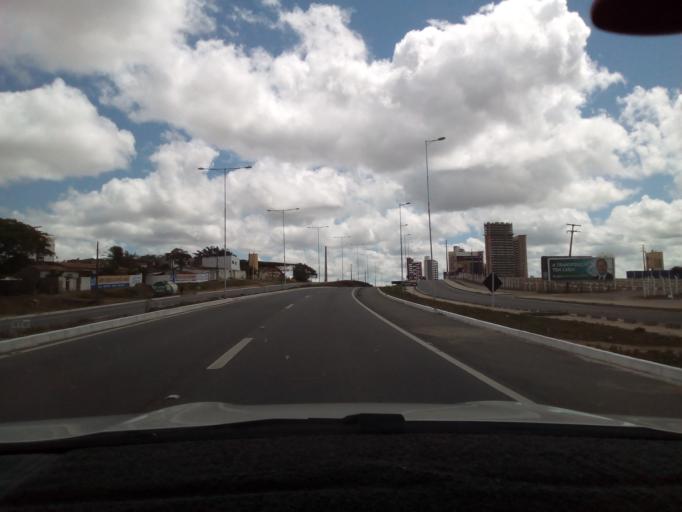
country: BR
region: Paraiba
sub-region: Campina Grande
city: Campina Grande
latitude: -7.2437
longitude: -35.8711
